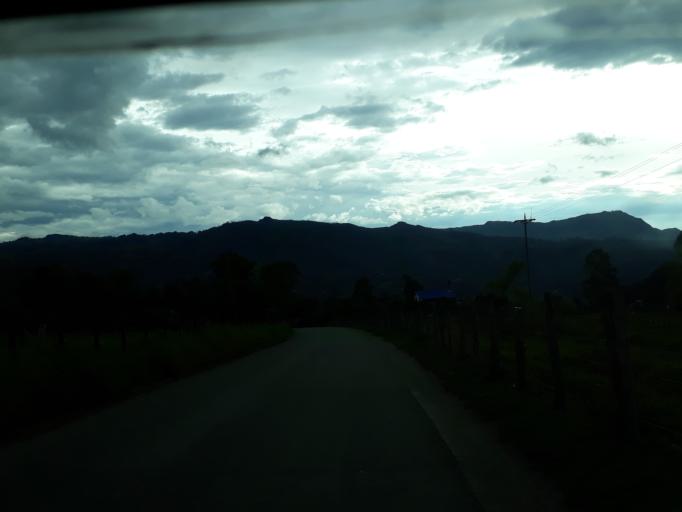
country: CO
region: Cundinamarca
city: Pacho
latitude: 5.1562
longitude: -74.1390
